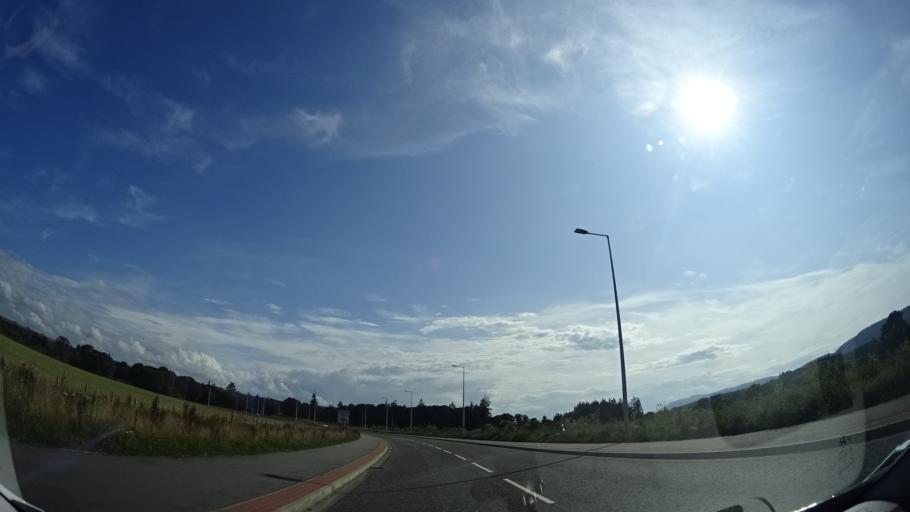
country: GB
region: Scotland
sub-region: Highland
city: Inverness
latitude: 57.4547
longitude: -4.2568
